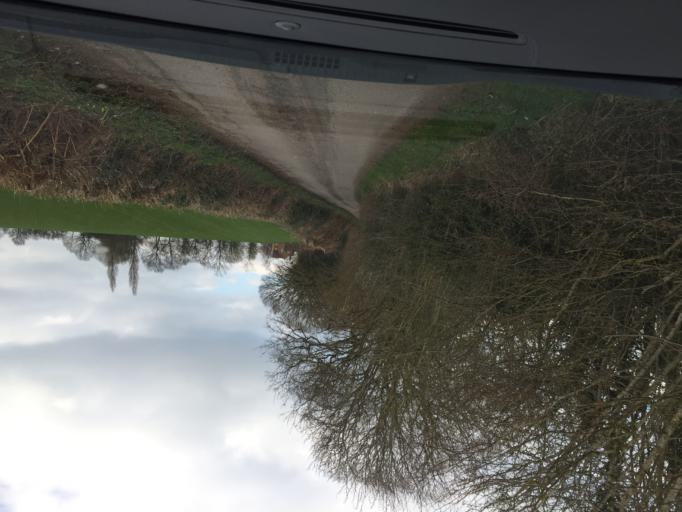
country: GB
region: England
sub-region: Solihull
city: Meriden
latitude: 52.4433
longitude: -1.5936
